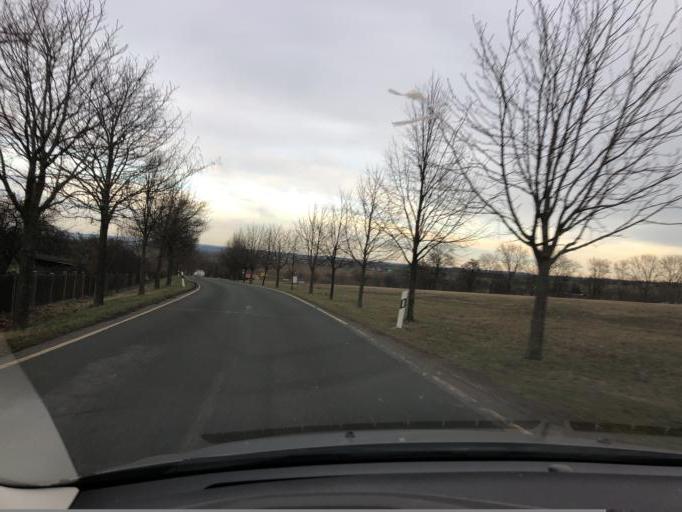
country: DE
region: Thuringia
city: Ramsla
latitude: 51.0361
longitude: 11.2840
